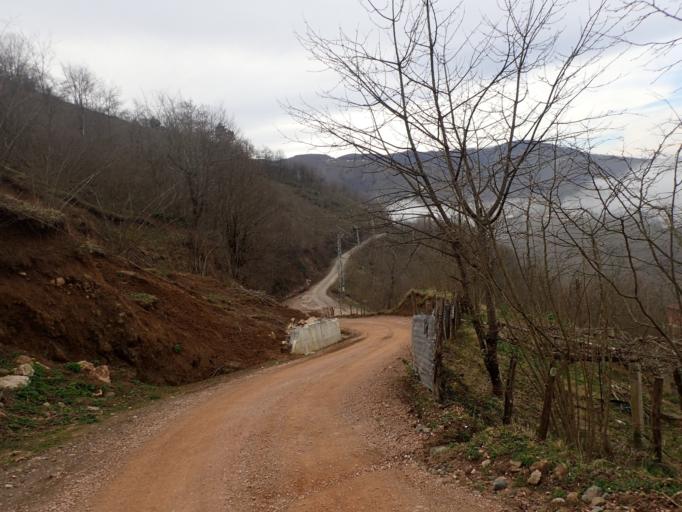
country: TR
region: Ordu
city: Camas
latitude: 40.8897
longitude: 37.5132
